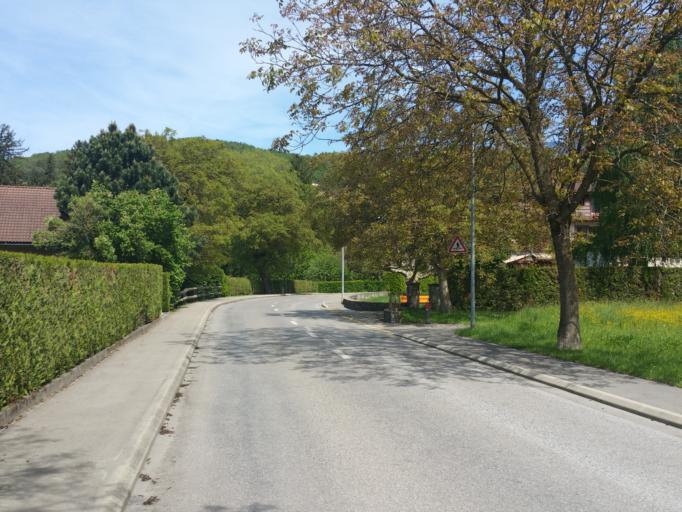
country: CH
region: Vaud
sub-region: Aigle District
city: Bex
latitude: 46.2468
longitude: 7.0221
